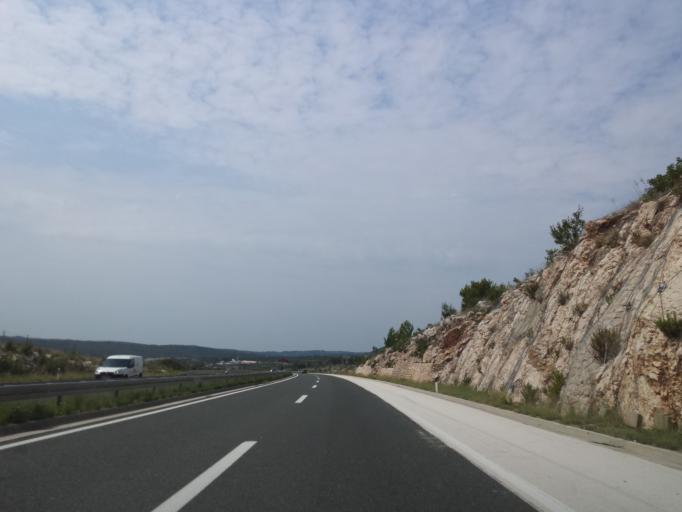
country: HR
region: Zadarska
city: Posedarje
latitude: 44.2199
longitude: 15.4676
